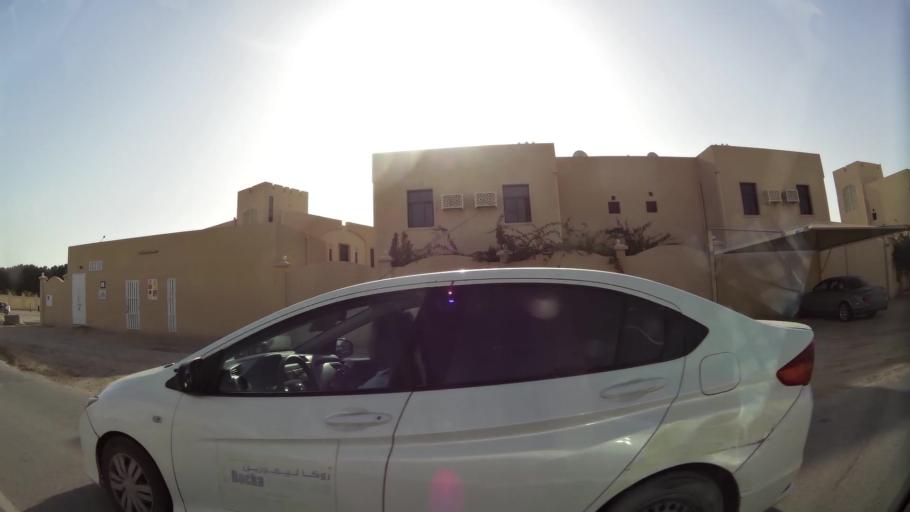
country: QA
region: Baladiyat ar Rayyan
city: Ar Rayyan
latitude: 25.3306
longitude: 51.4415
